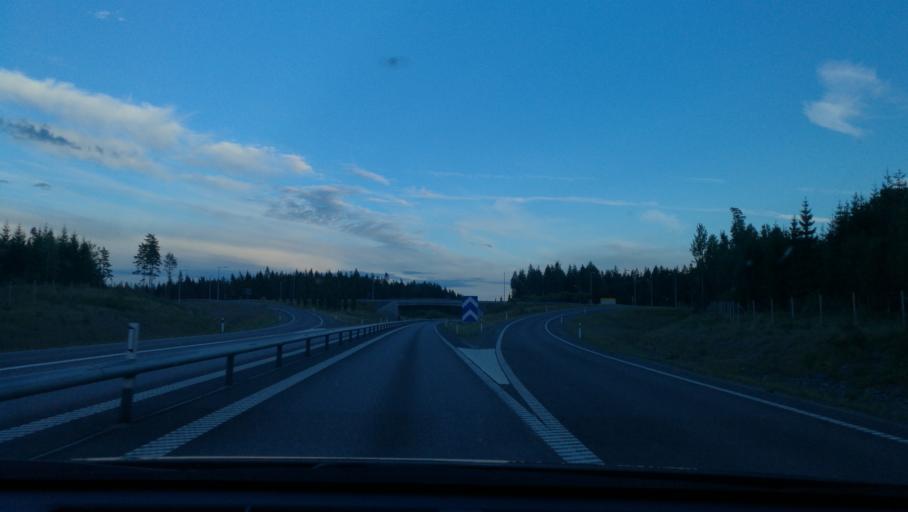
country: SE
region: Soedermanland
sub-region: Katrineholms Kommun
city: Katrineholm
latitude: 58.9956
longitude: 16.2577
